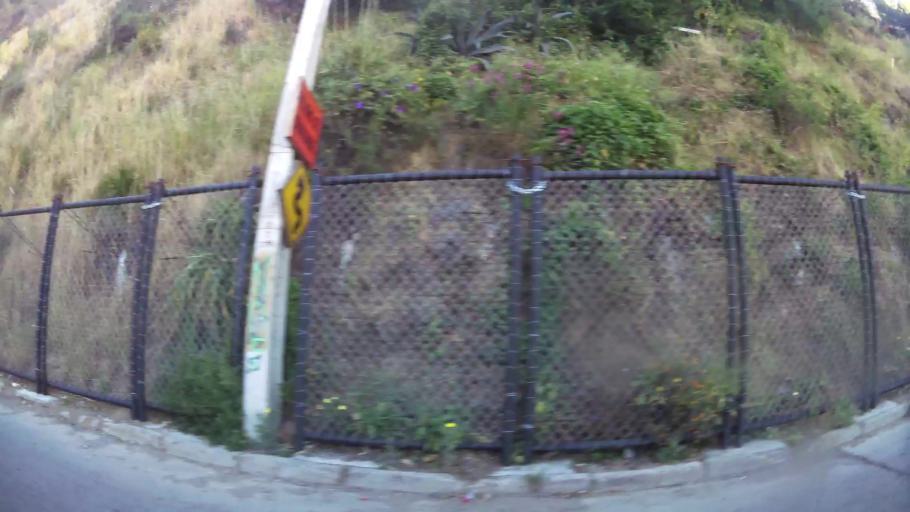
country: CL
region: Valparaiso
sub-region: Provincia de Valparaiso
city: Valparaiso
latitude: -33.0542
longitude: -71.6153
